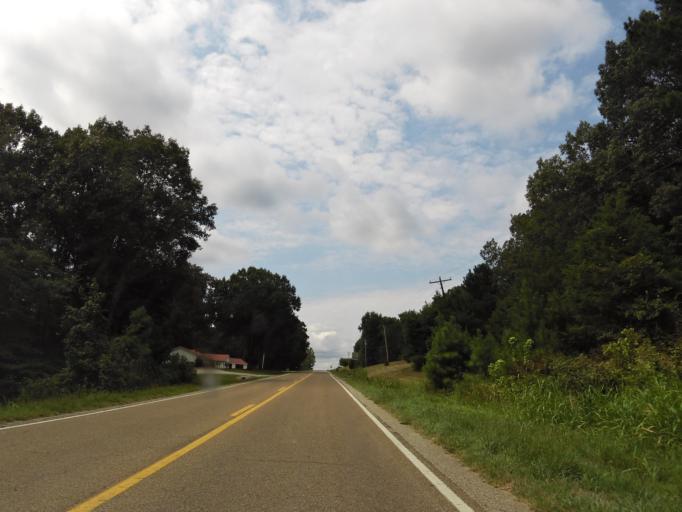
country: US
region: Tennessee
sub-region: Henderson County
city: Lexington
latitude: 35.5098
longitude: -88.3184
